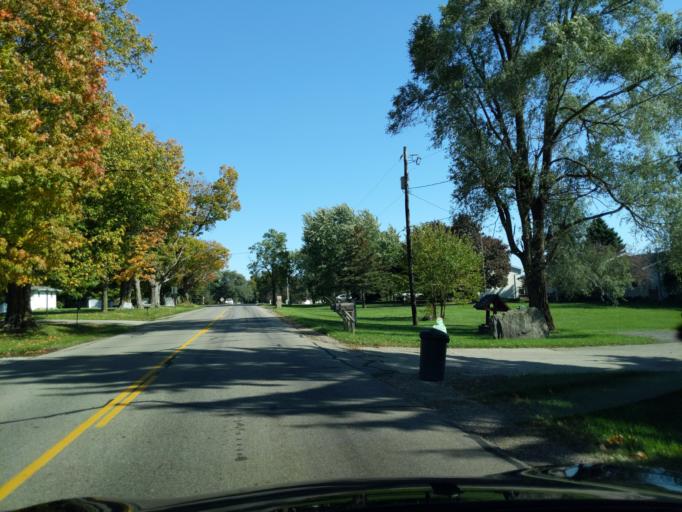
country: US
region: Michigan
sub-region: Eaton County
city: Charlotte
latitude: 42.5821
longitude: -84.7993
